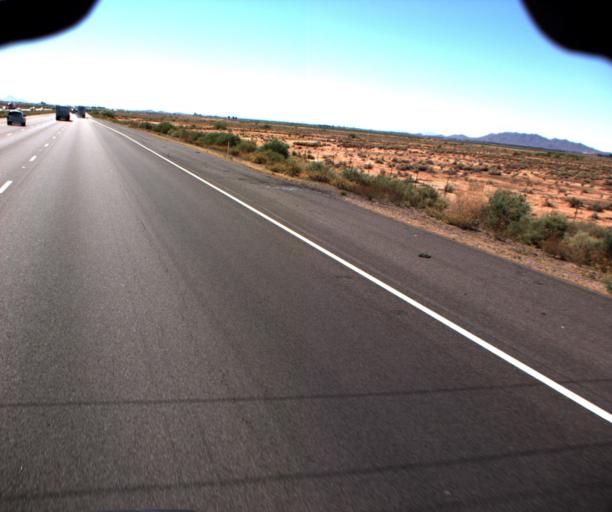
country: US
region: Arizona
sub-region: Pinal County
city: Casa Grande
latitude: 32.9337
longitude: -111.6974
